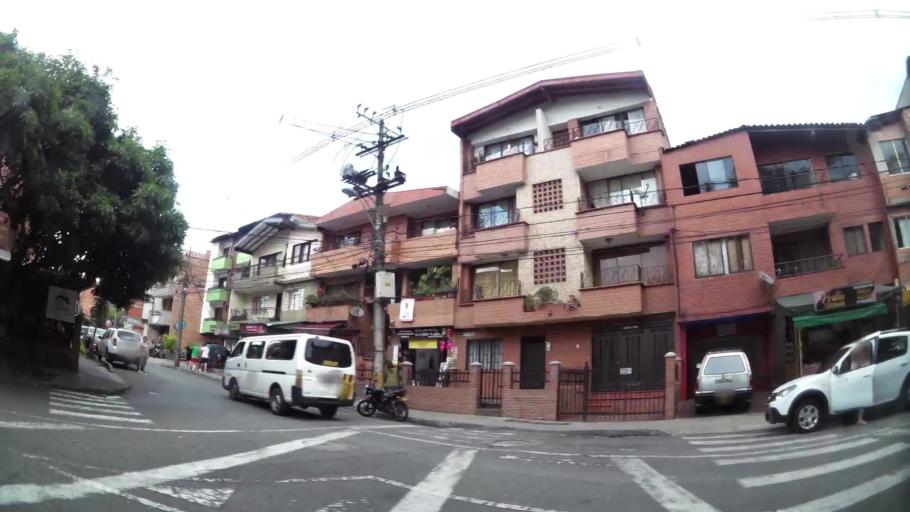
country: CO
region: Antioquia
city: Envigado
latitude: 6.1646
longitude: -75.5906
